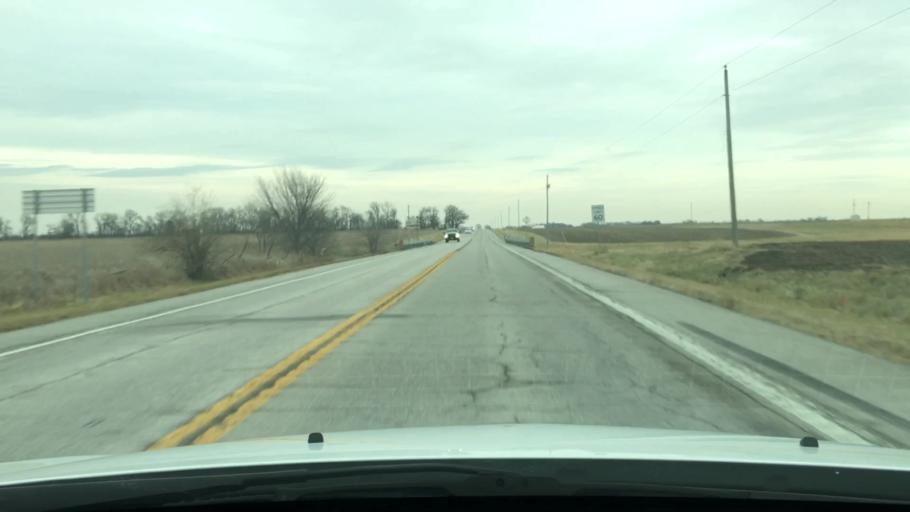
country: US
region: Missouri
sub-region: Audrain County
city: Vandalia
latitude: 39.2810
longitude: -91.6408
